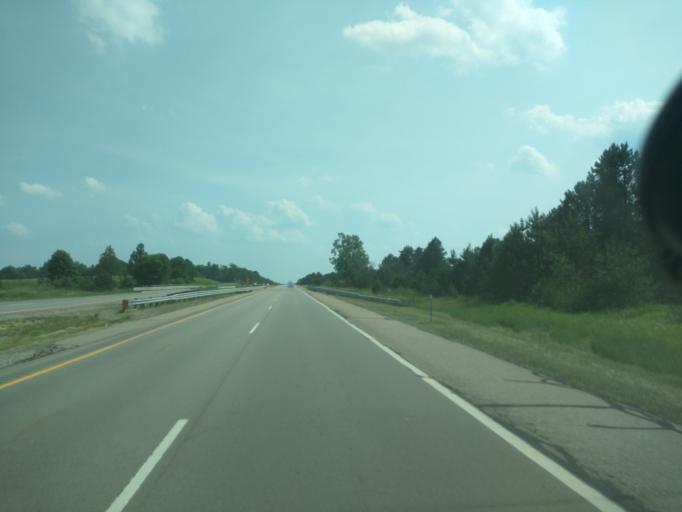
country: US
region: Michigan
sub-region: Ingham County
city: Leslie
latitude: 42.3798
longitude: -84.4292
